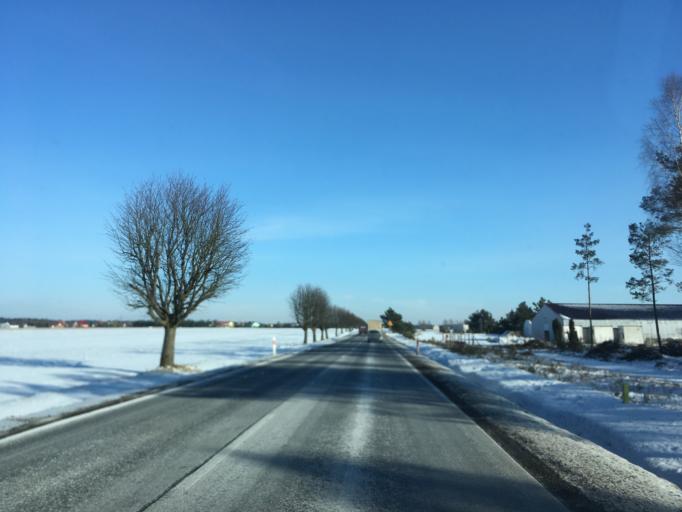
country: PL
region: Pomeranian Voivodeship
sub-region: Powiat koscierski
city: Lipusz
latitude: 54.1327
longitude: 17.8438
